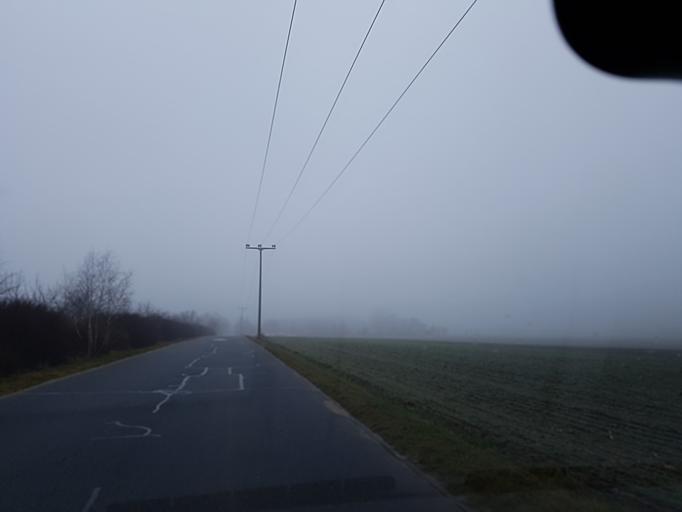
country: DE
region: Brandenburg
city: Finsterwalde
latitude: 51.6474
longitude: 13.7185
